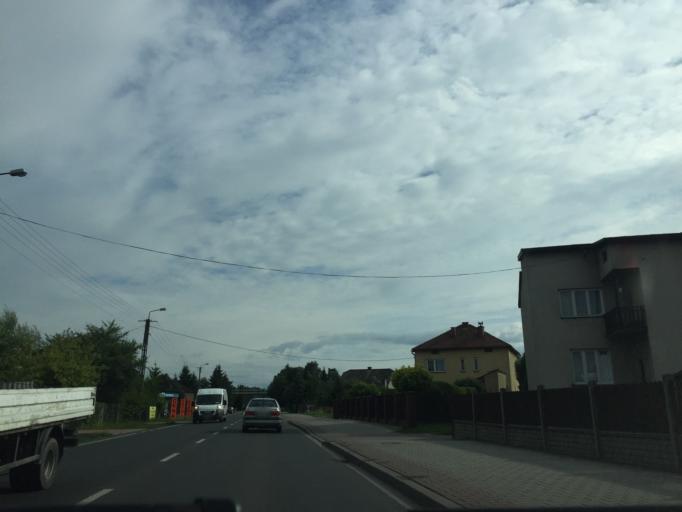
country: PL
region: Lesser Poland Voivodeship
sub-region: Powiat oswiecimski
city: Zaborze
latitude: 50.0288
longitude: 19.2532
